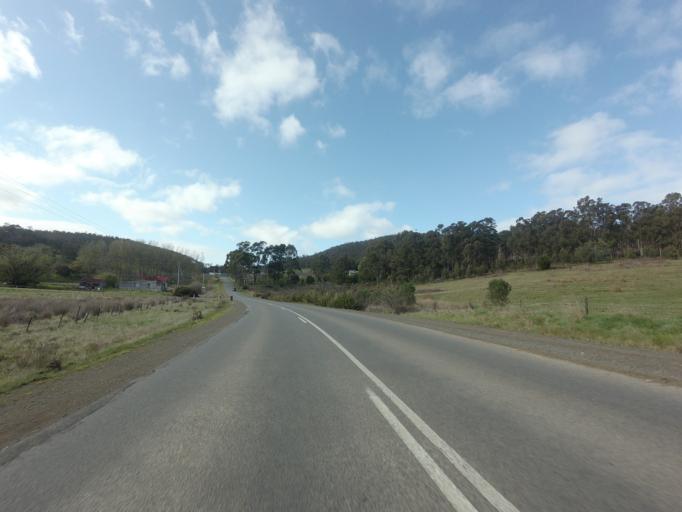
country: AU
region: Tasmania
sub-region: Huon Valley
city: Geeveston
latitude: -43.1688
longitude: 146.9408
